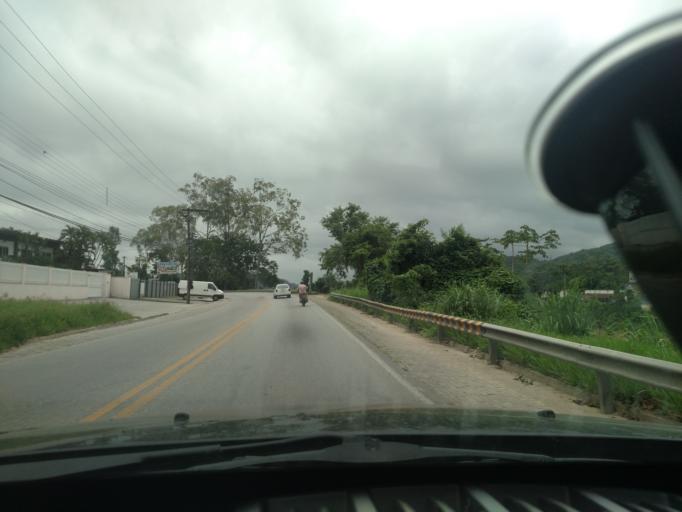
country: BR
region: Santa Catarina
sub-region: Gaspar
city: Gaspar
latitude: -26.9209
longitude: -48.9713
